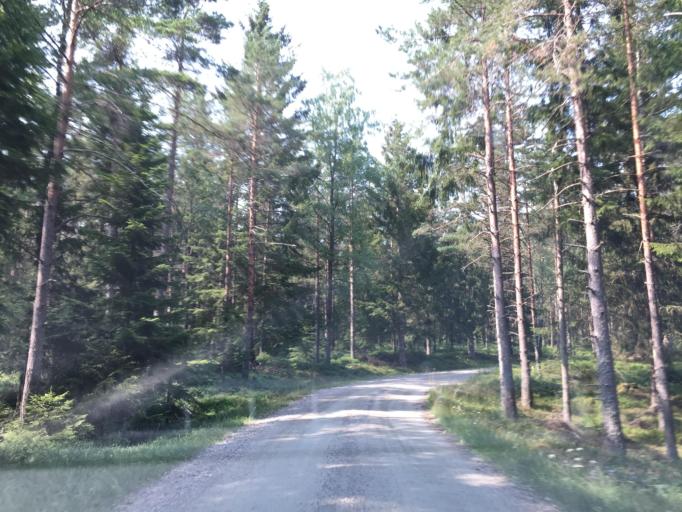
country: SE
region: Vaestra Goetaland
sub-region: Lilla Edets Kommun
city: Lilla Edet
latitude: 58.2476
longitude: 12.0876
